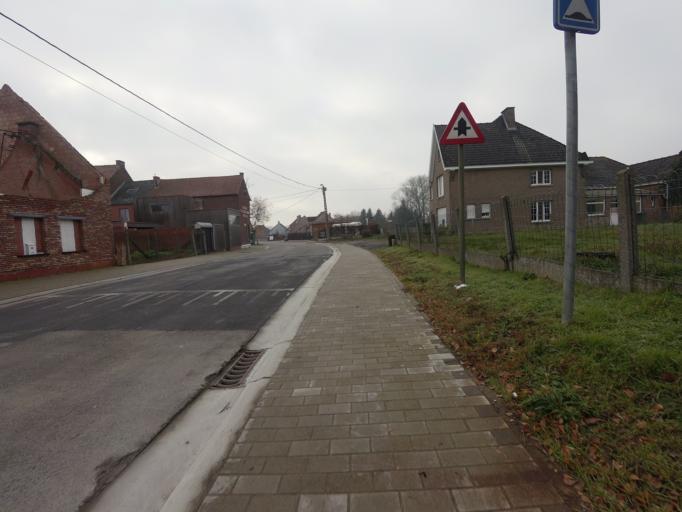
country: BE
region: Flanders
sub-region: Provincie Vlaams-Brabant
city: Galmaarden
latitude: 50.8095
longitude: 3.9622
